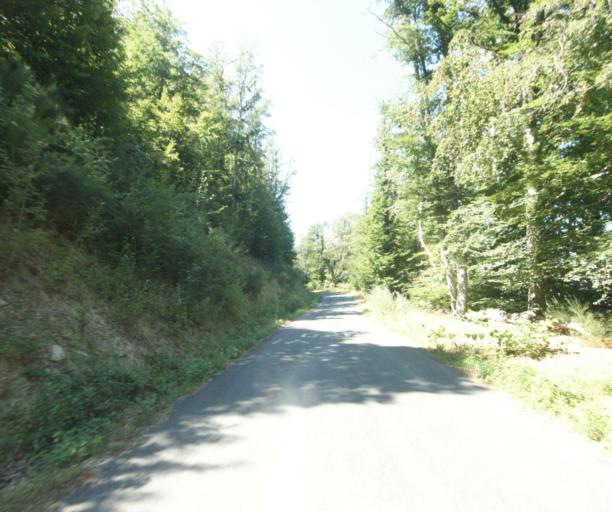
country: FR
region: Rhone-Alpes
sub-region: Departement du Rhone
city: Courzieu
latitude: 45.7244
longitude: 4.5567
